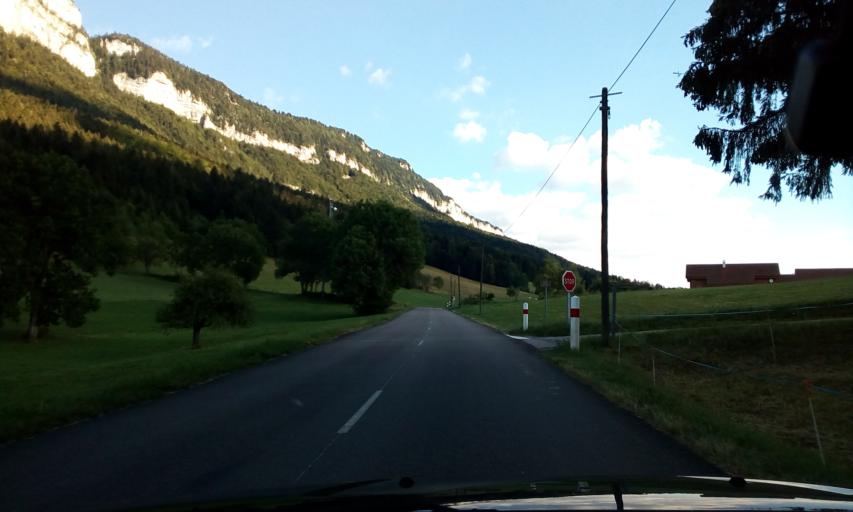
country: FR
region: Rhone-Alpes
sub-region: Departement de l'Isere
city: Meaudre
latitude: 45.0715
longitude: 5.4584
